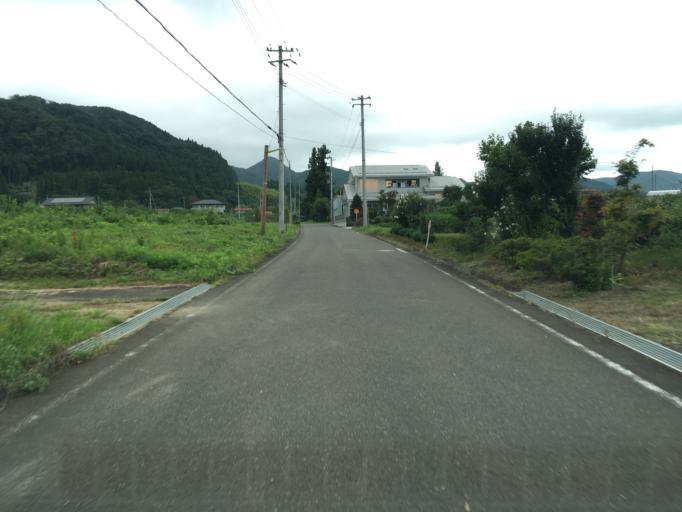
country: JP
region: Fukushima
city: Fukushima-shi
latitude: 37.7810
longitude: 140.3831
